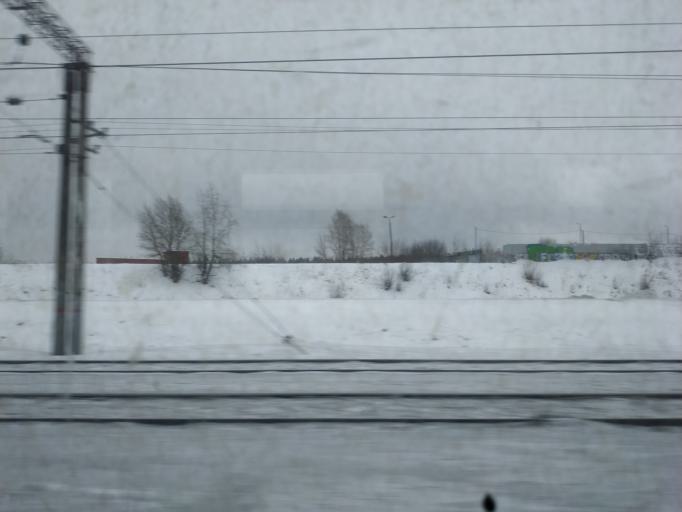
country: RU
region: Moskovskaya
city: Biryulevo Zapadnoye
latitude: 55.5983
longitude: 37.6265
